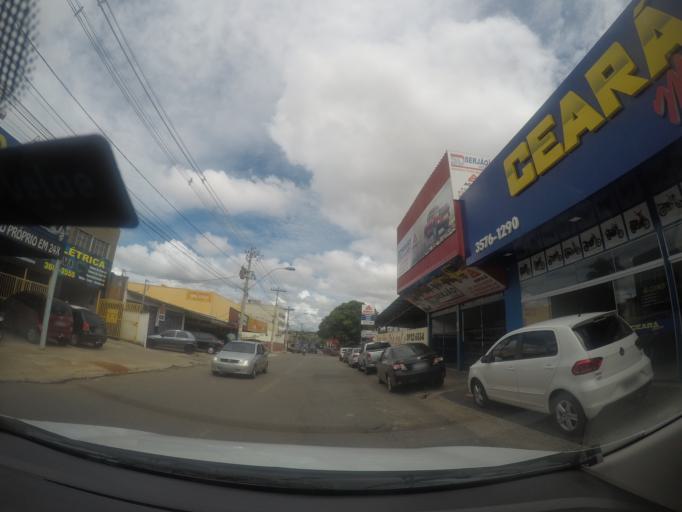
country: BR
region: Goias
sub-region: Goiania
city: Goiania
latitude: -16.6615
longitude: -49.3067
